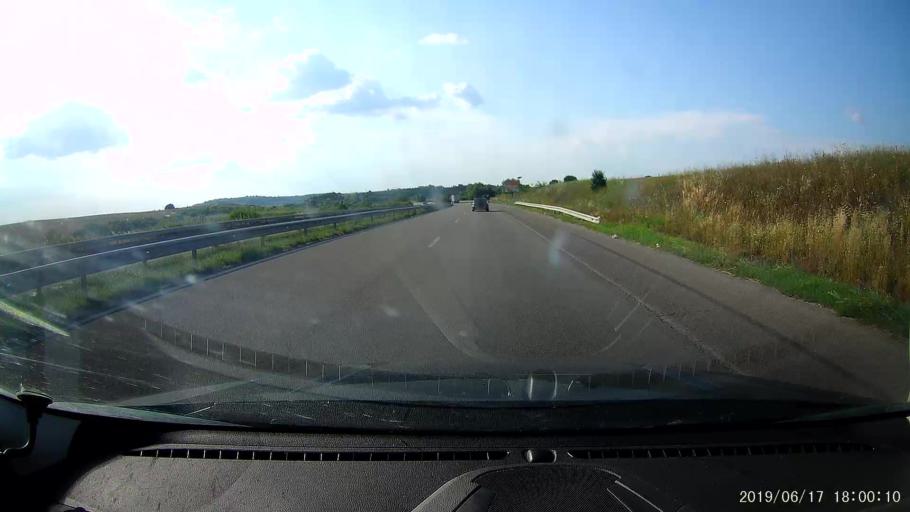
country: BG
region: Khaskovo
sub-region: Obshtina Svilengrad
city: Svilengrad
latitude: 41.7324
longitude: 26.2832
